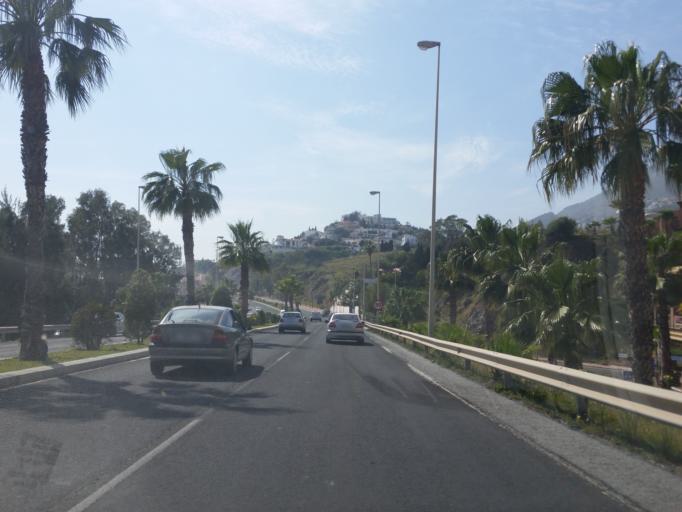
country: ES
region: Andalusia
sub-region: Provincia de Malaga
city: Benalmadena
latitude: 36.5811
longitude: -4.5554
